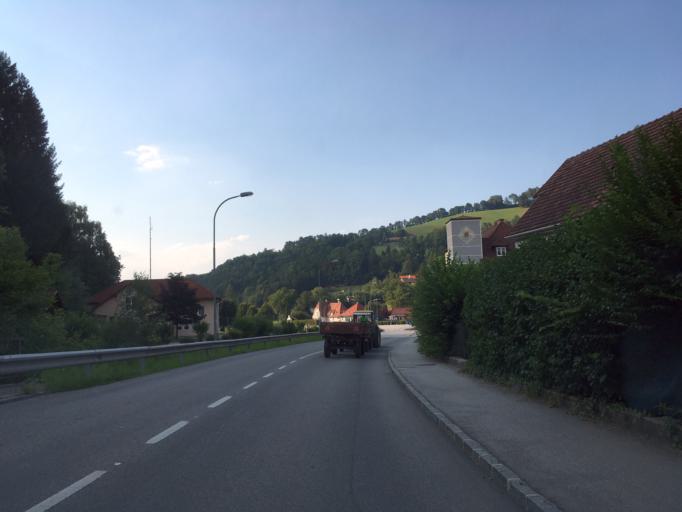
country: AT
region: Lower Austria
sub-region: Politischer Bezirk Neunkirchen
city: Edlitz
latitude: 47.5977
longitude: 16.1397
